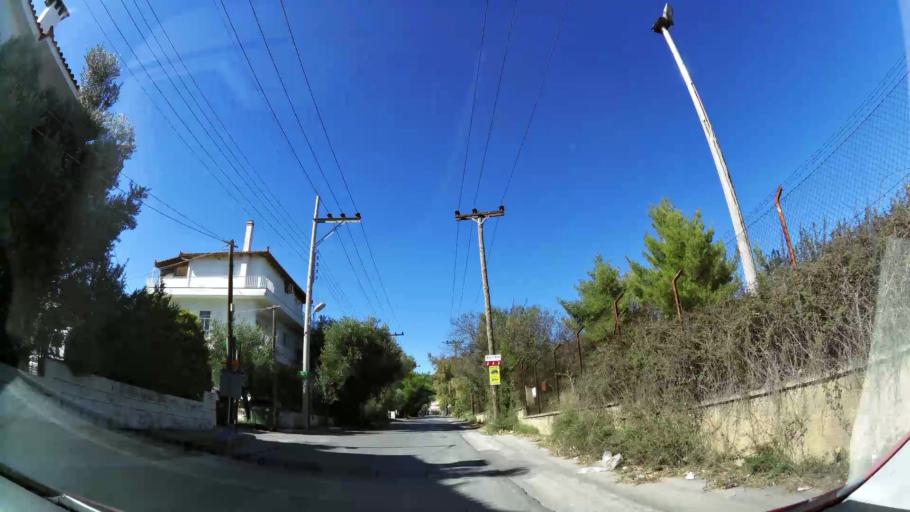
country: GR
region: Attica
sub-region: Nomarchia Anatolikis Attikis
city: Leondarion
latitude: 37.9918
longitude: 23.8515
